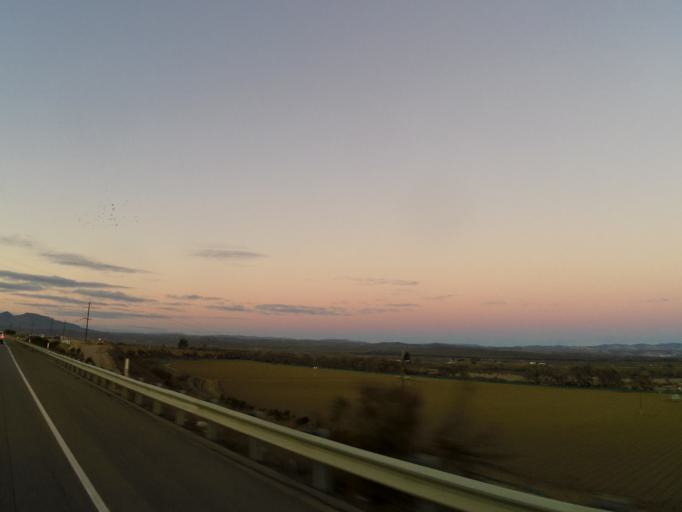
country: US
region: California
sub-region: Monterey County
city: King City
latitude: 36.2317
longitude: -121.1740
